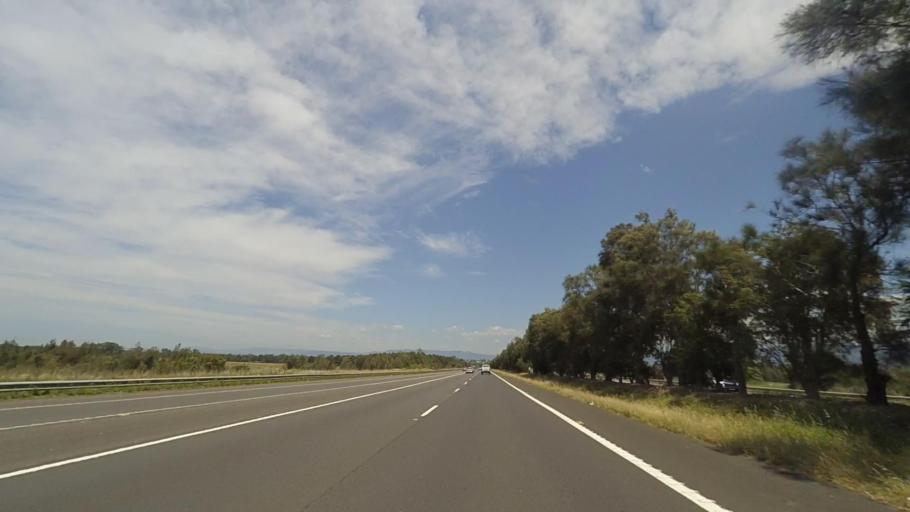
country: AU
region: New South Wales
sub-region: Wollongong
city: Berkeley
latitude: -34.4764
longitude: 150.8289
